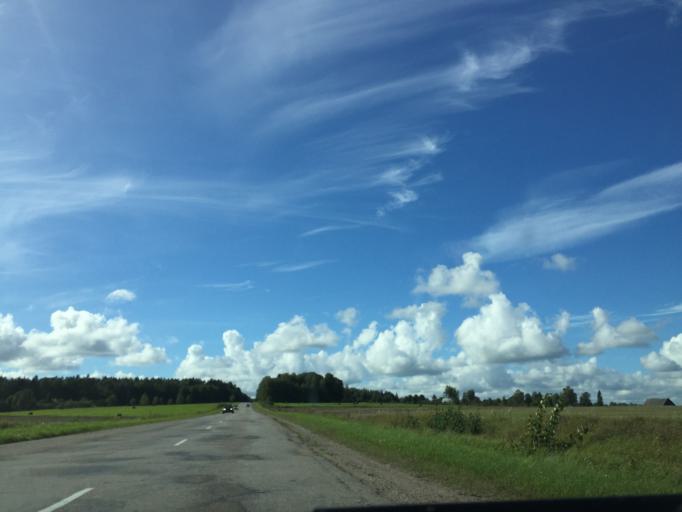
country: LV
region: Kuldigas Rajons
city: Kuldiga
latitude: 56.9874
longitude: 21.7913
